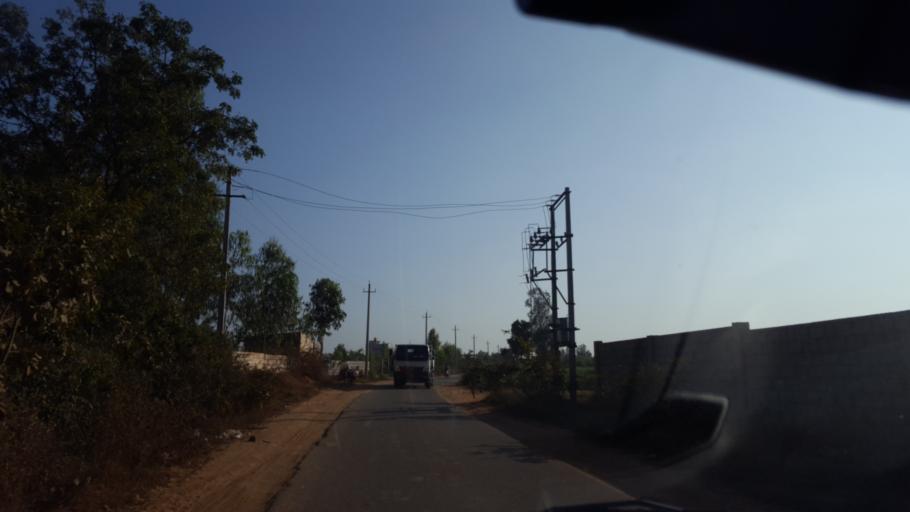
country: IN
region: Karnataka
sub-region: Bangalore Rural
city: Hoskote
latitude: 12.9263
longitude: 77.7564
